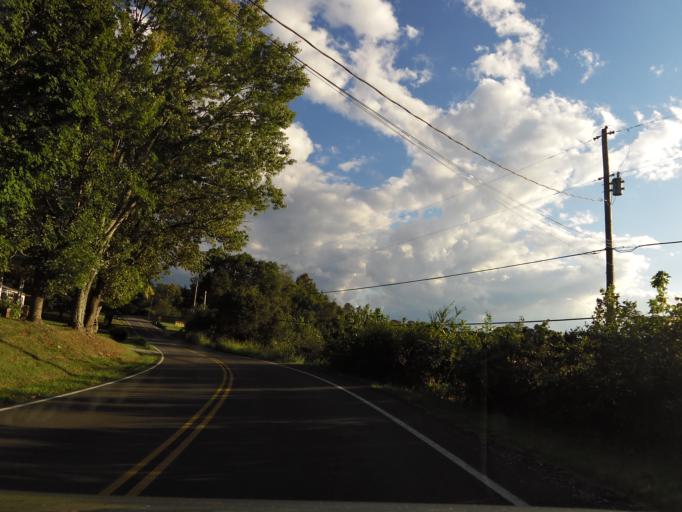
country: US
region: Tennessee
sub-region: Grainger County
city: Rutledge
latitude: 36.2448
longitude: -83.5278
